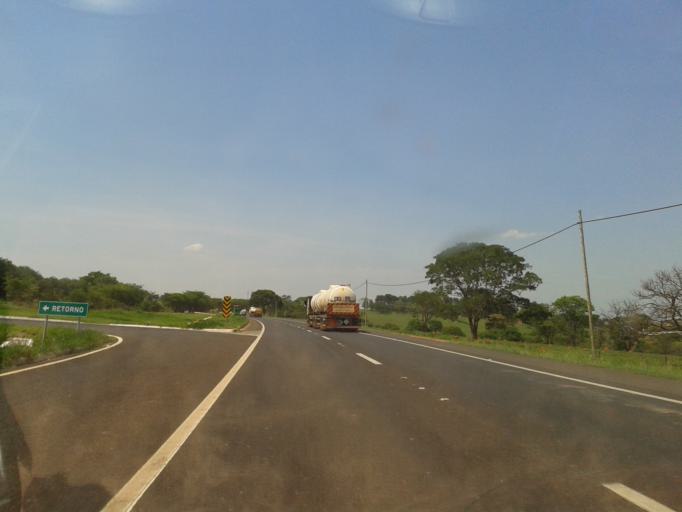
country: BR
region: Minas Gerais
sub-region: Monte Alegre De Minas
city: Monte Alegre de Minas
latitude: -18.8722
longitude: -48.5984
